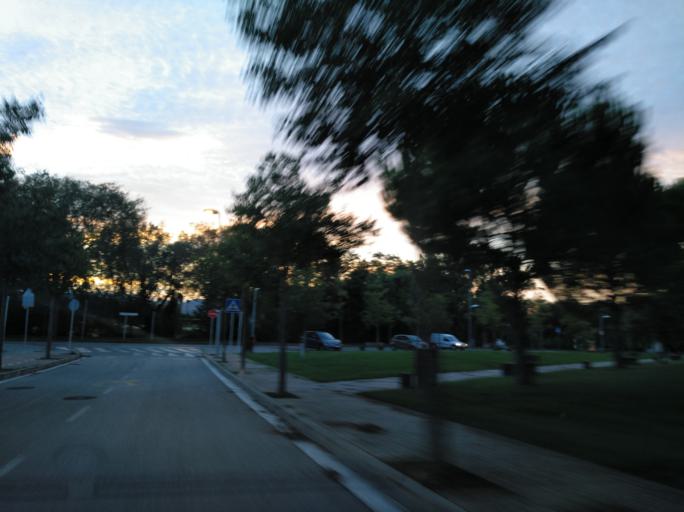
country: ES
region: Catalonia
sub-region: Provincia de Girona
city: Vilablareix
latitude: 41.9536
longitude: 2.7930
